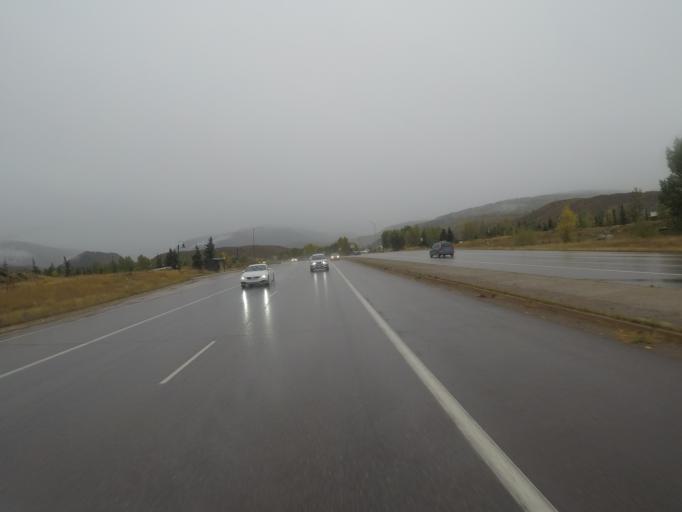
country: US
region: Colorado
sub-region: Pitkin County
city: Aspen
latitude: 39.2256
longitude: -106.8666
